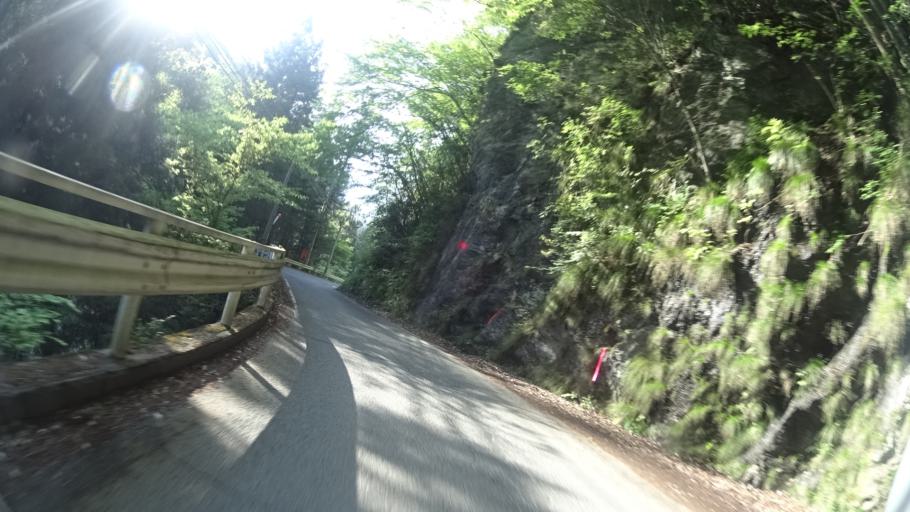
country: JP
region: Tokushima
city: Ikedacho
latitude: 33.8764
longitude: 133.9392
